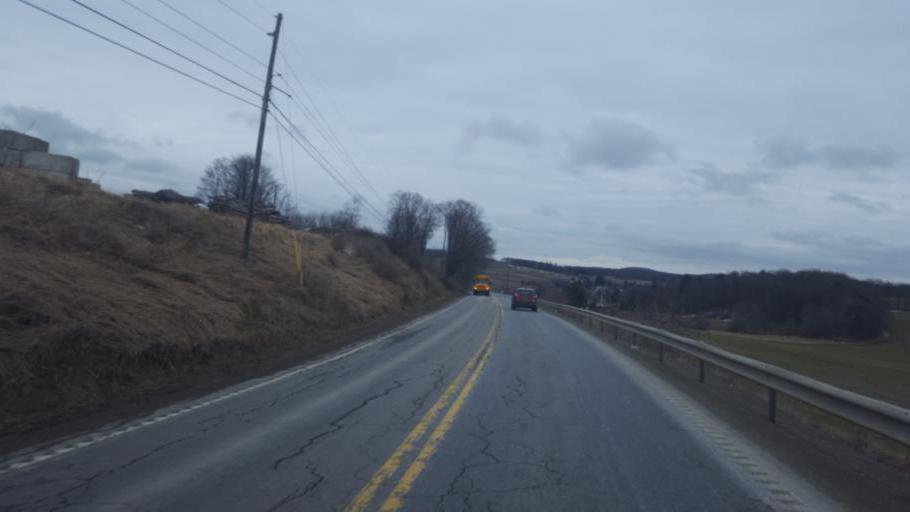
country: US
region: Pennsylvania
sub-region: Potter County
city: Galeton
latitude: 41.8982
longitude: -77.7784
